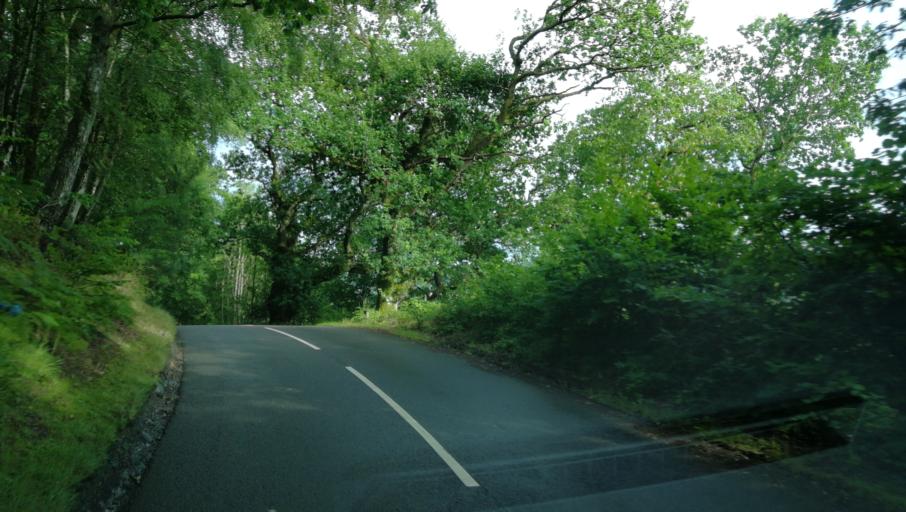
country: GB
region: Scotland
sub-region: Stirling
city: Callander
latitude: 56.2266
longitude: -4.3213
